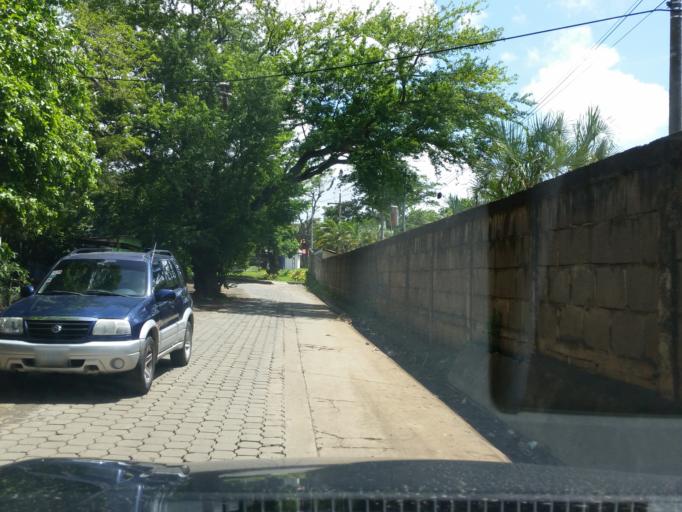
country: NI
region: Managua
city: Managua
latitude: 12.0826
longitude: -86.2314
